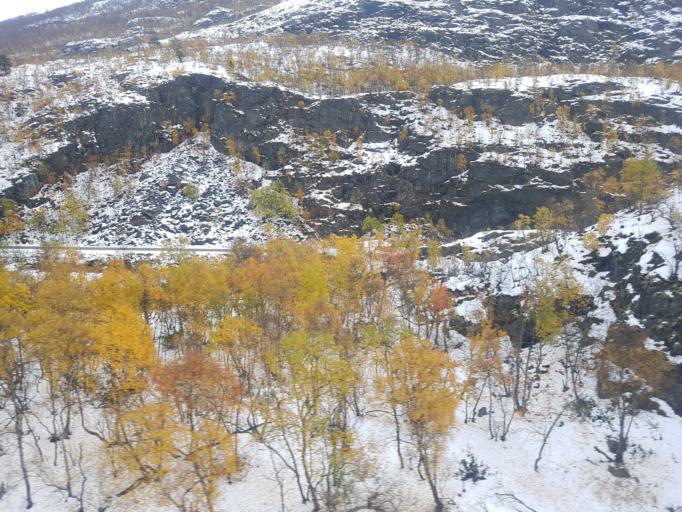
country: NO
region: Sor-Trondelag
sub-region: Oppdal
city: Oppdal
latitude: 62.3899
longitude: 9.6371
